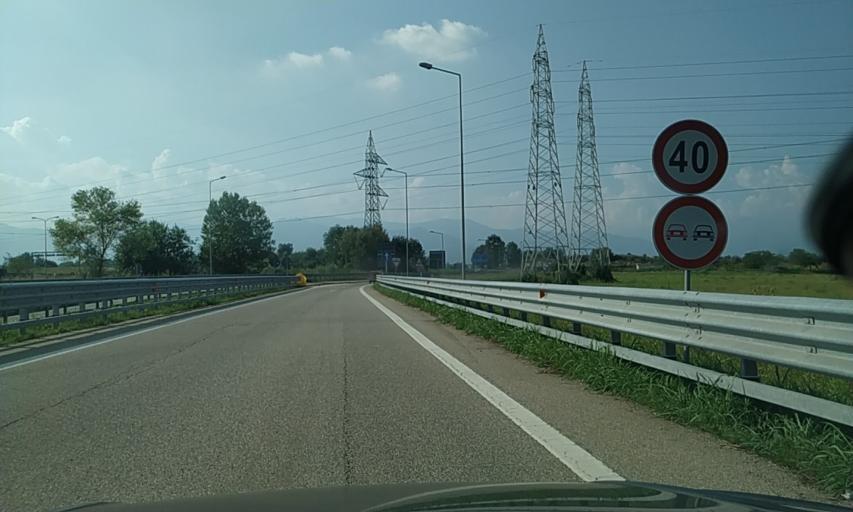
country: IT
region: Piedmont
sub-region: Provincia di Torino
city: Savonera
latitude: 45.1072
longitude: 7.5970
